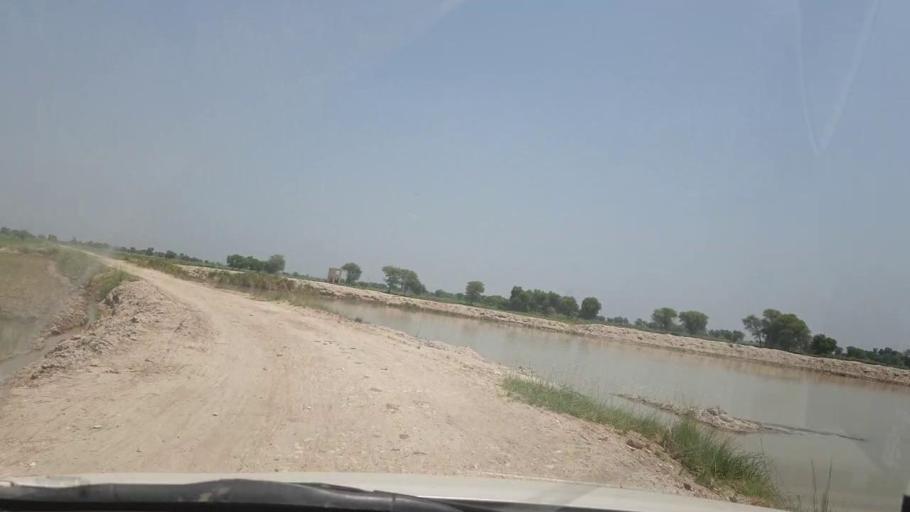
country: PK
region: Sindh
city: Lakhi
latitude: 27.8649
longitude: 68.7191
